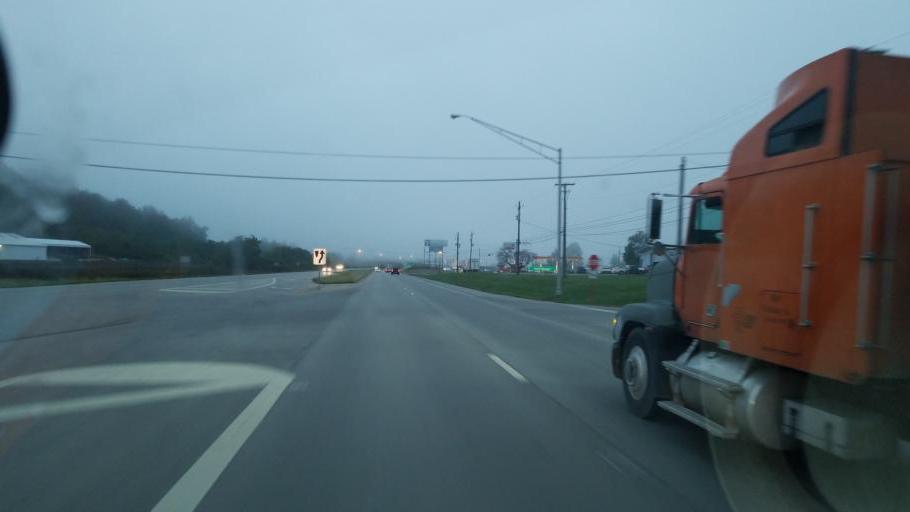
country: US
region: Ohio
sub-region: Pike County
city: Piketon
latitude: 39.0228
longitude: -83.0265
